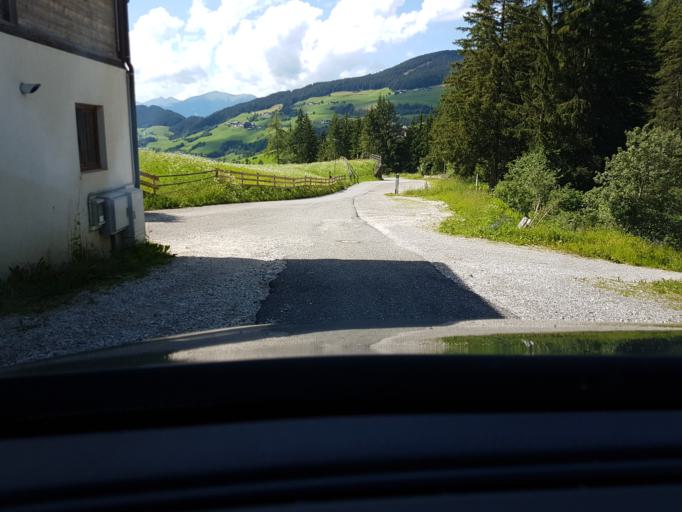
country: IT
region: Trentino-Alto Adige
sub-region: Bolzano
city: San Pietro
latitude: 46.6341
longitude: 11.7284
